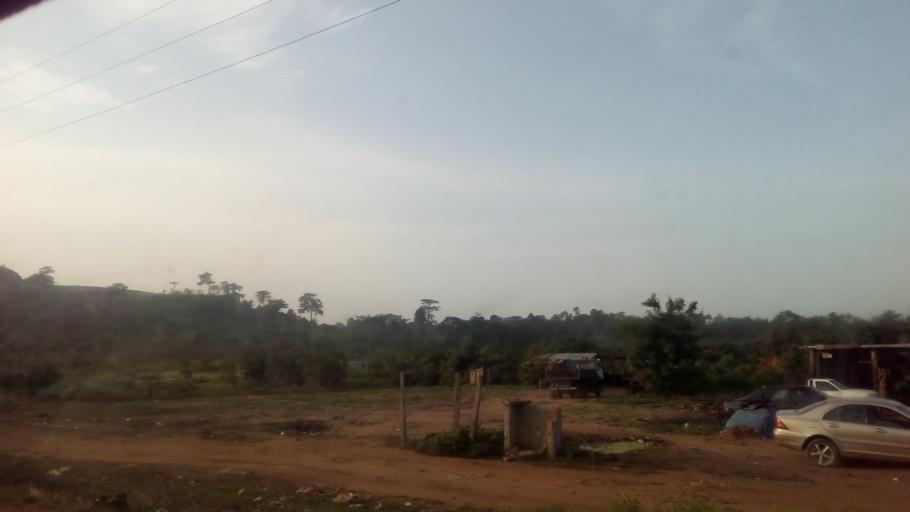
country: CI
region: Dix-Huit Montagnes
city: Duekoue
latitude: 6.7519
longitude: -7.3605
